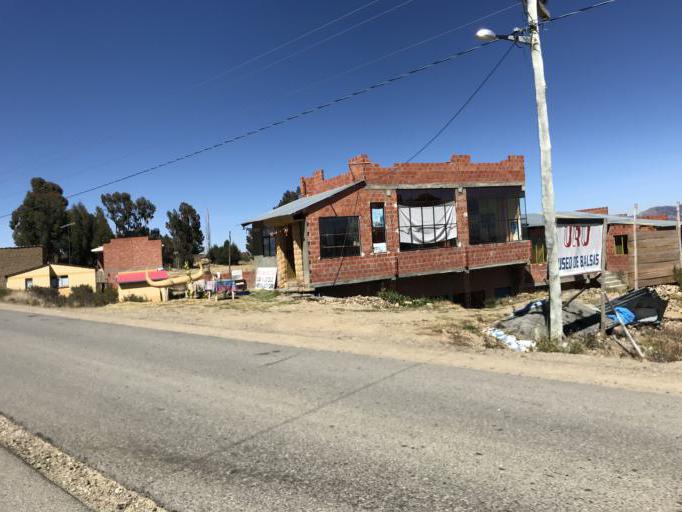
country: BO
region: La Paz
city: Huatajata
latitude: -16.2150
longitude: -68.6753
